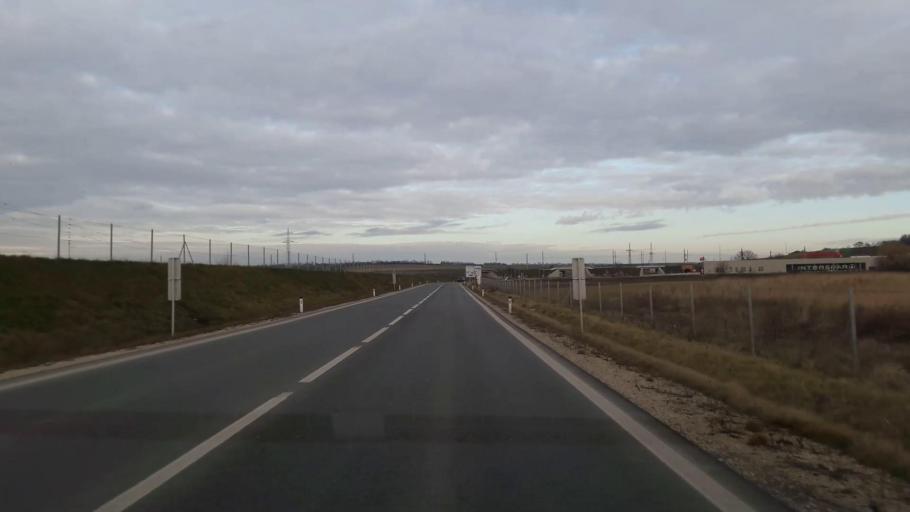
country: AT
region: Lower Austria
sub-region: Politischer Bezirk Mistelbach
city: Mistelbach
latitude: 48.5583
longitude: 16.5568
